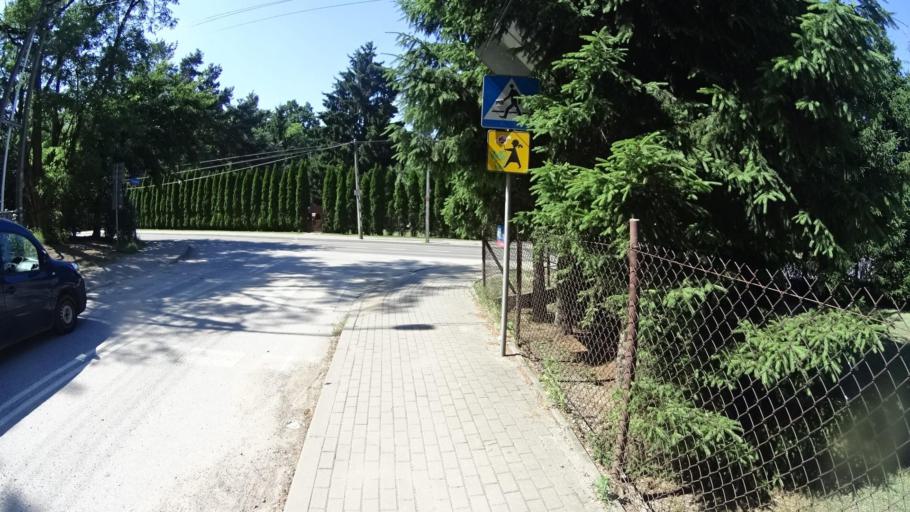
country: PL
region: Masovian Voivodeship
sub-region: Warszawa
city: Bialoleka
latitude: 52.3413
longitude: 20.9421
